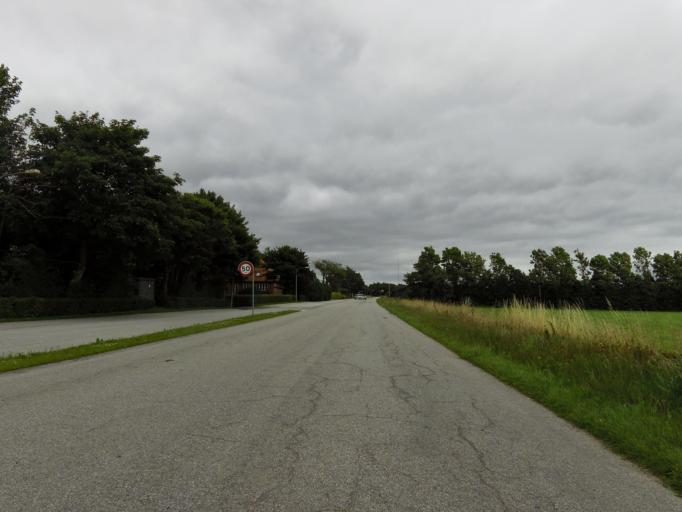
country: DK
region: South Denmark
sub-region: Haderslev Kommune
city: Gram
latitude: 55.2688
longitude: 9.1717
